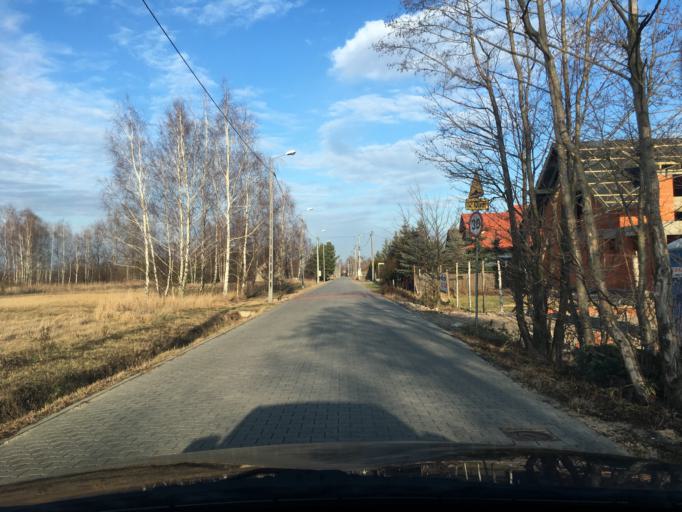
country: PL
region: Masovian Voivodeship
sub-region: Powiat piaseczynski
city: Lesznowola
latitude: 52.0298
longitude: 20.9365
